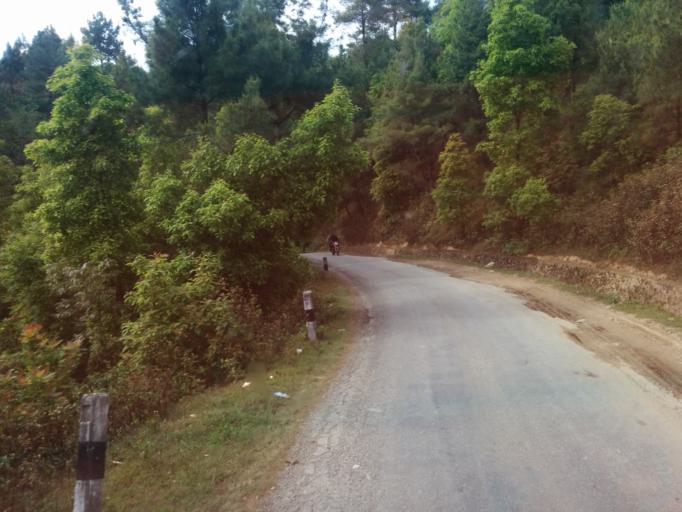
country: NP
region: Central Region
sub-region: Bagmati Zone
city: Nagarkot
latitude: 27.7100
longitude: 85.4883
